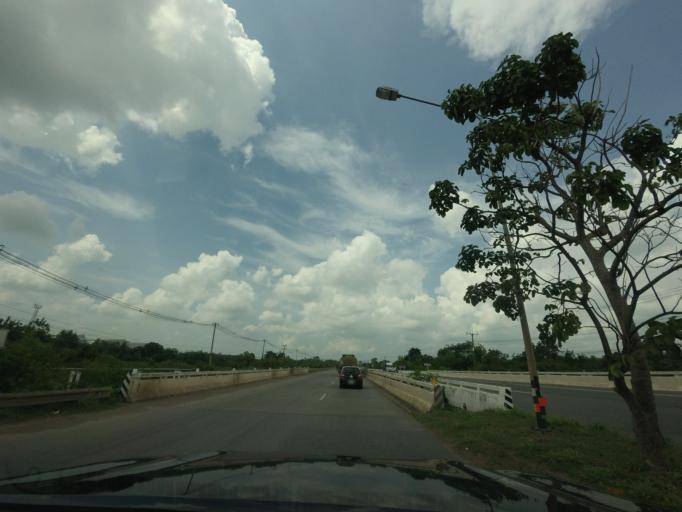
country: TH
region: Khon Kaen
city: Nong Ruea
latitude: 16.4920
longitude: 102.4269
